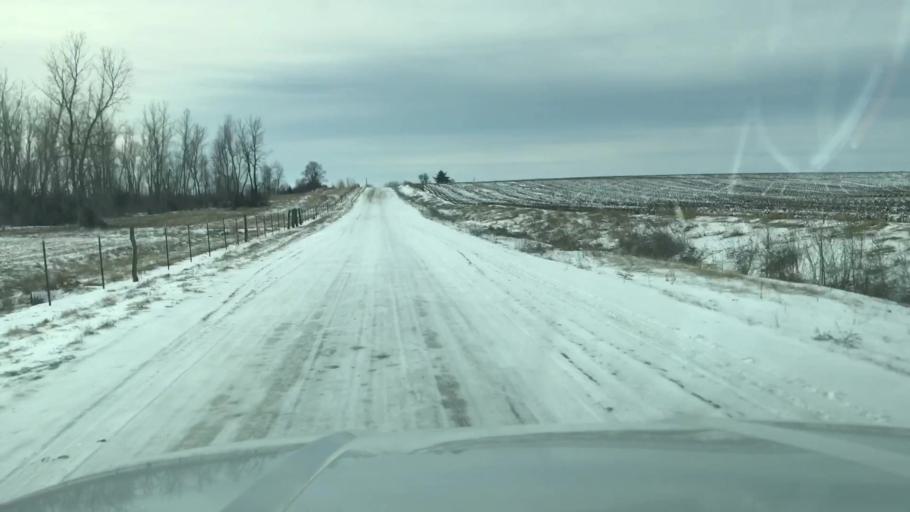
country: US
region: Missouri
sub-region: Holt County
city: Mound City
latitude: 40.1356
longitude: -95.0696
